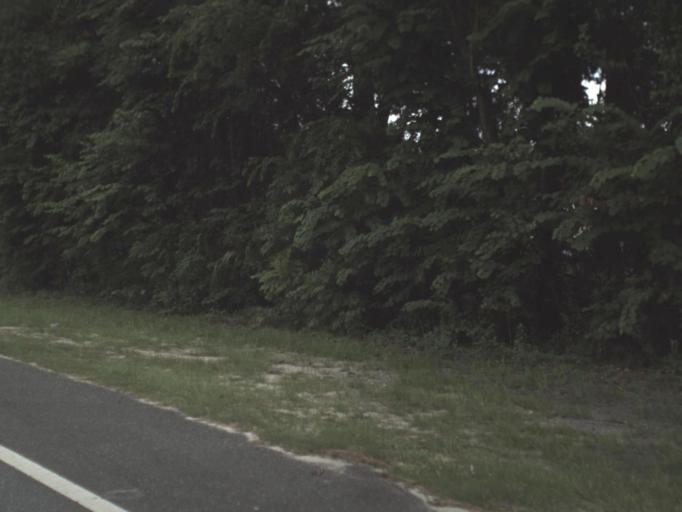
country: US
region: Florida
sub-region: Lafayette County
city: Mayo
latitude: 29.9611
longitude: -82.9231
